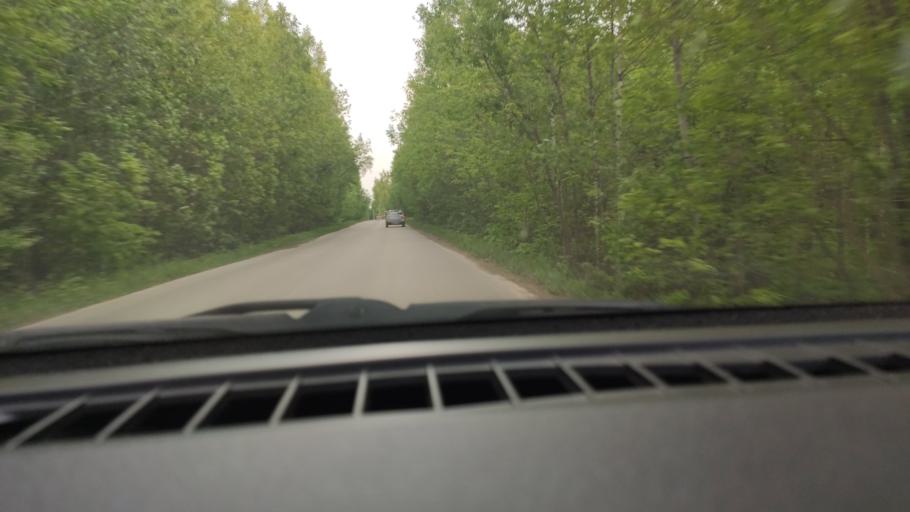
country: RU
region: Perm
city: Kondratovo
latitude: 58.0626
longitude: 56.0028
